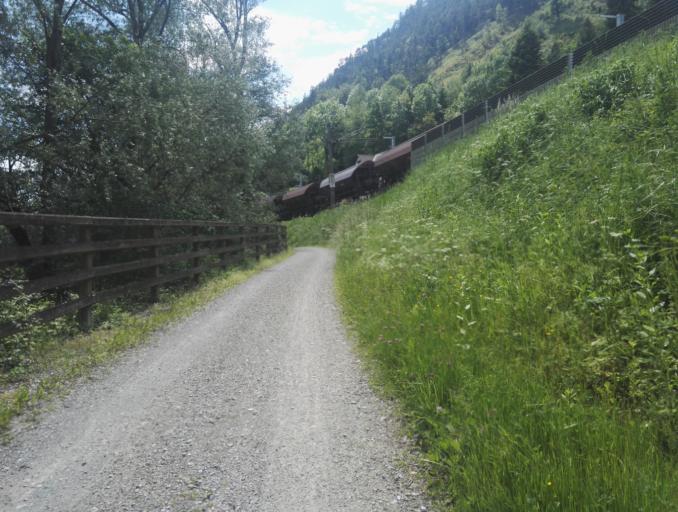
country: AT
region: Styria
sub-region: Politischer Bezirk Graz-Umgebung
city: Deutschfeistritz
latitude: 47.1753
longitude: 15.3196
